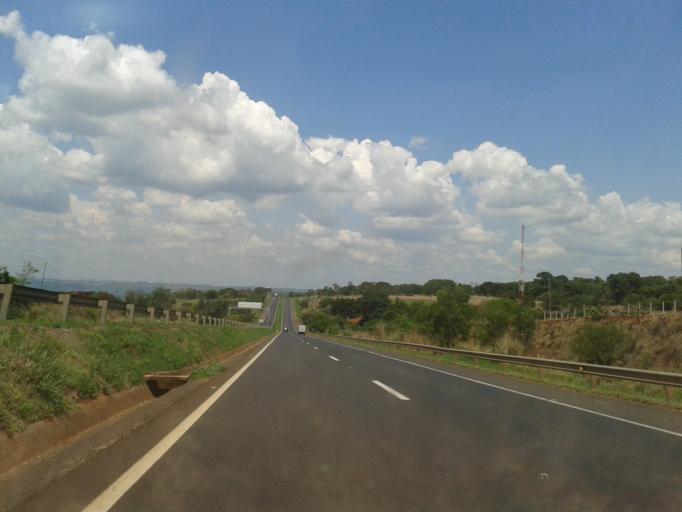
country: BR
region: Minas Gerais
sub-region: Araguari
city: Araguari
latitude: -18.7051
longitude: -48.1907
